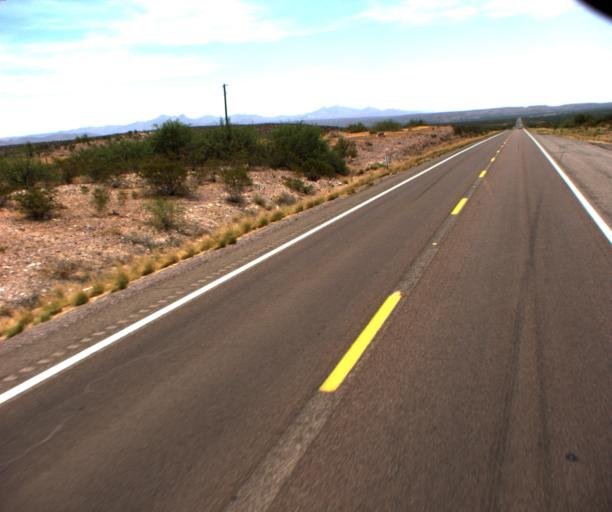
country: US
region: Arizona
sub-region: Graham County
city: Bylas
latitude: 33.1975
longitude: -110.1827
